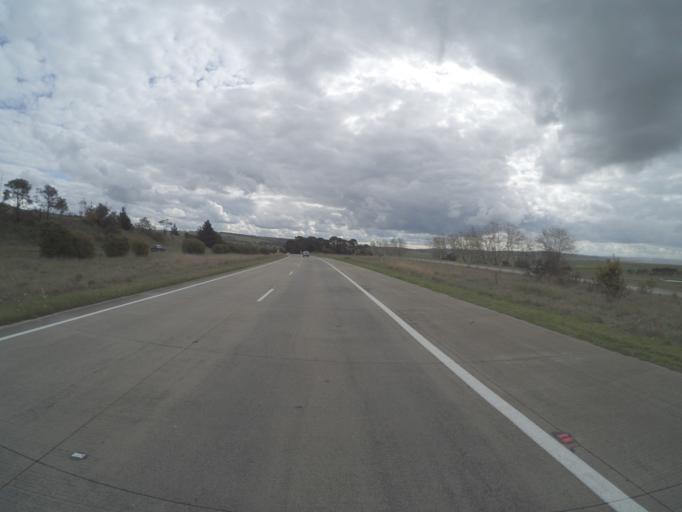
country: AU
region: New South Wales
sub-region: Goulburn Mulwaree
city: Goulburn
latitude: -34.8066
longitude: 149.5329
